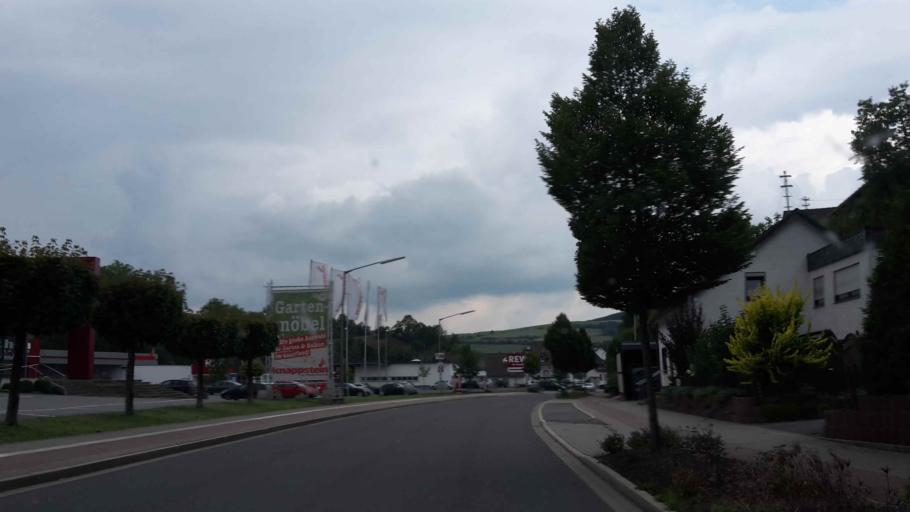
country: DE
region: North Rhine-Westphalia
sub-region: Regierungsbezirk Arnsberg
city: Lennestadt
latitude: 51.1497
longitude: 8.0629
